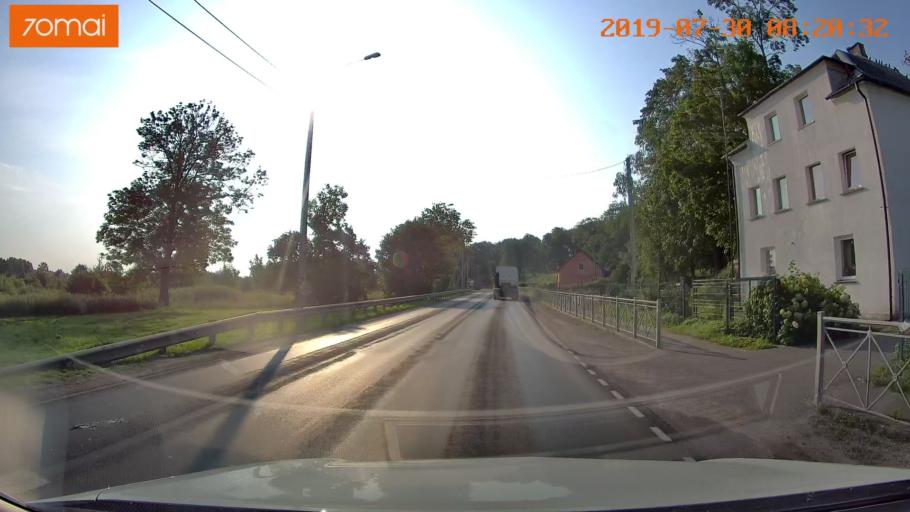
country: RU
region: Kaliningrad
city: Chernyakhovsk
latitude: 54.6266
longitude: 21.5174
